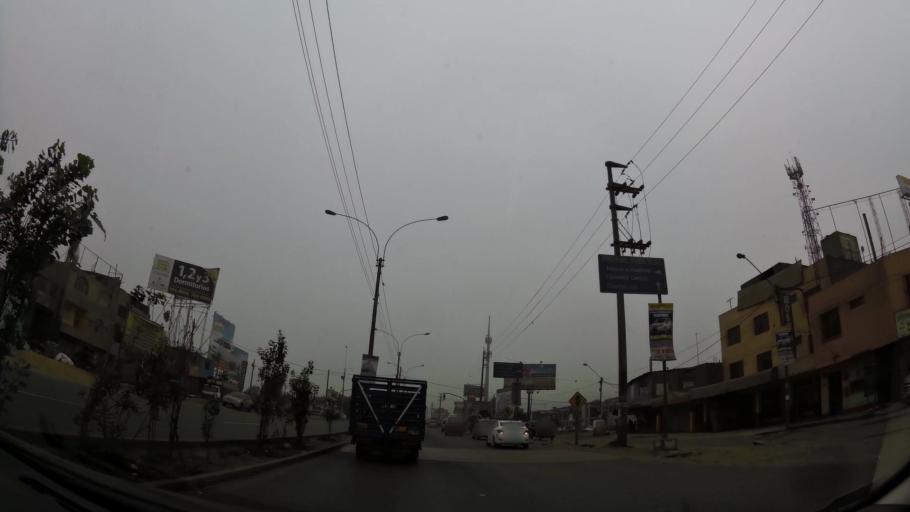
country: PE
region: Lima
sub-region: Lima
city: Santa Maria
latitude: -12.0005
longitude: -76.8394
